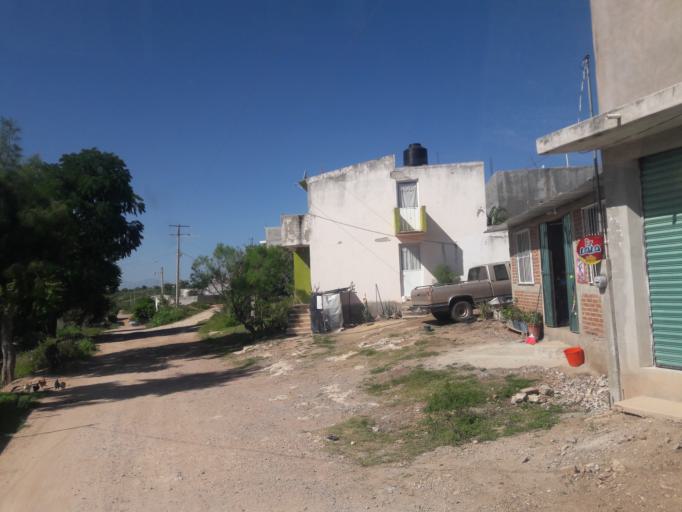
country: MX
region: Oaxaca
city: Ciudad de Huajuapam de Leon
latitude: 17.8049
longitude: -97.8047
